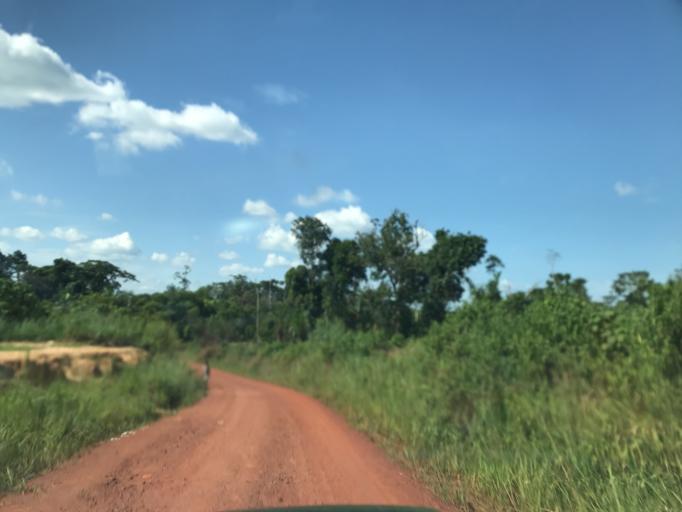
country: CD
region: Eastern Province
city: Kisangani
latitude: 1.2095
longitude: 25.2643
